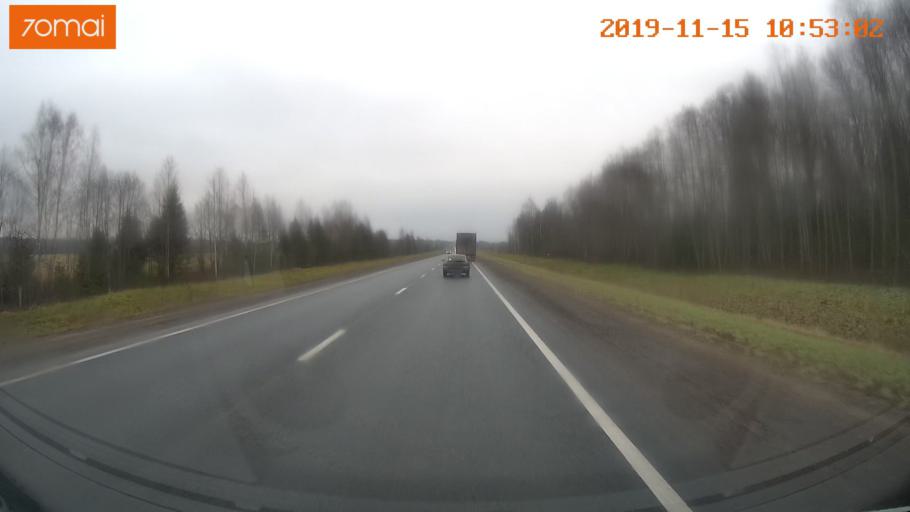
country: RU
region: Vologda
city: Chebsara
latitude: 59.1711
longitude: 38.7457
